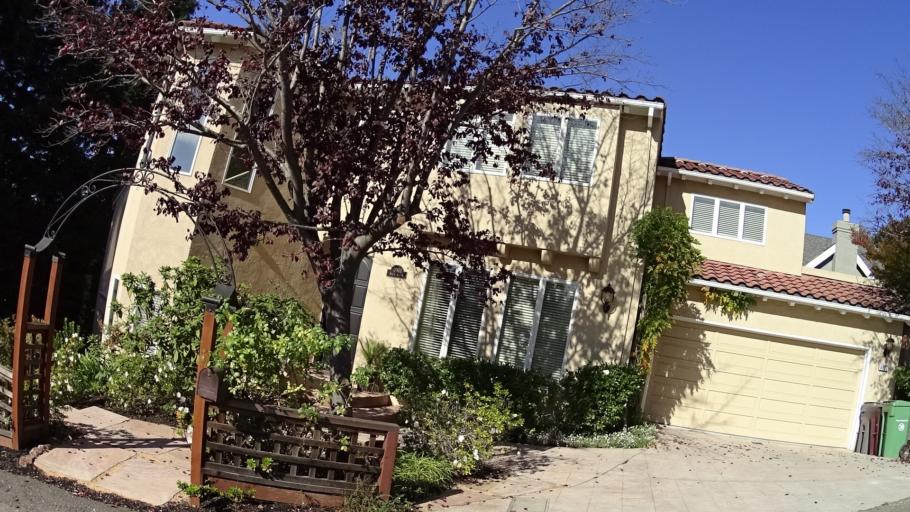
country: US
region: California
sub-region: Alameda County
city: Piedmont
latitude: 37.8417
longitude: -122.2209
